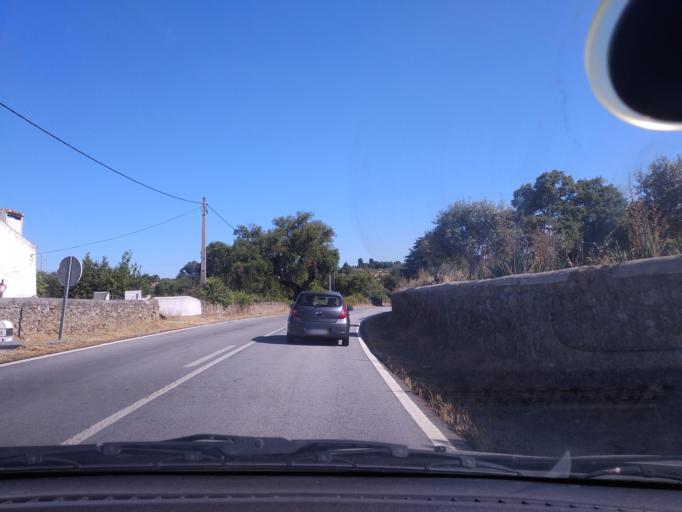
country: PT
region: Portalegre
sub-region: Nisa
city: Nisa
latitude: 39.4981
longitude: -7.6431
